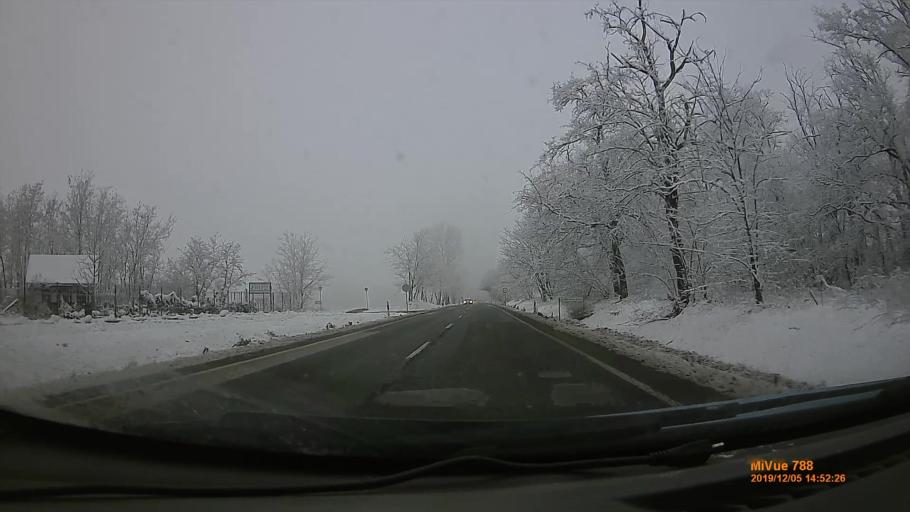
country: HU
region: Szabolcs-Szatmar-Bereg
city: Nyirtelek
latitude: 48.0013
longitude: 21.6447
